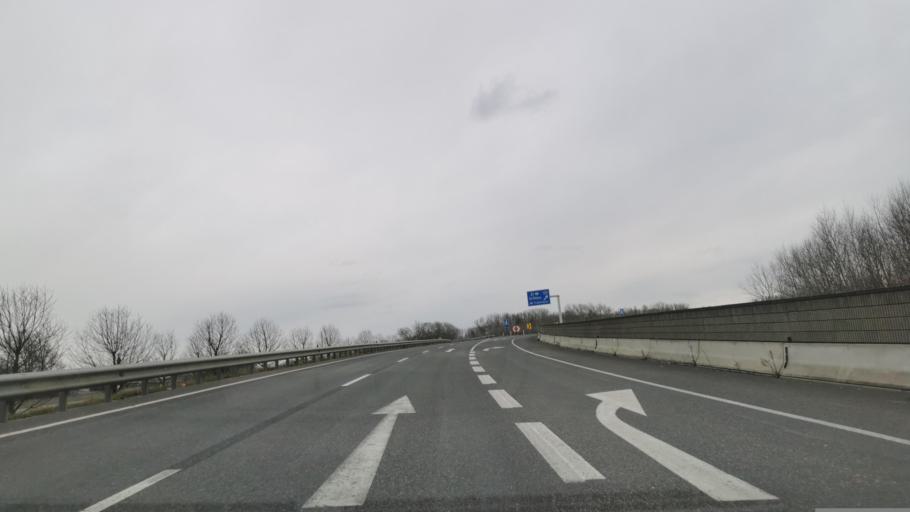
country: AT
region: Lower Austria
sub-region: Politischer Bezirk Krems
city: Grafenegg
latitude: 48.4082
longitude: 15.7384
